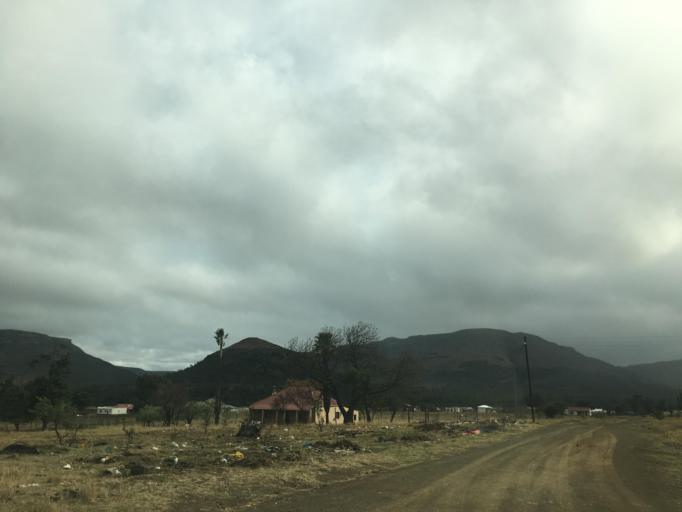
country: ZA
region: Eastern Cape
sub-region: Chris Hani District Municipality
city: Cala
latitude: -31.5226
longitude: 27.6917
